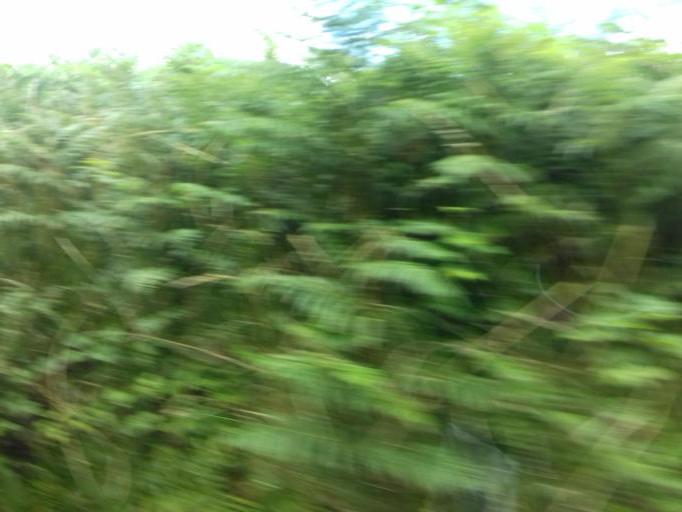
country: IE
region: Leinster
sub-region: County Carlow
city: Bagenalstown
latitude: 52.6270
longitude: -6.8225
